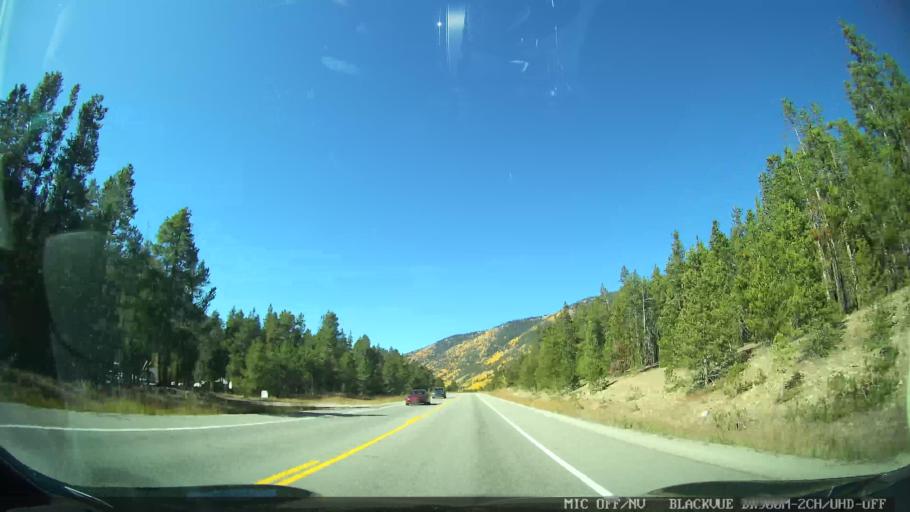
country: US
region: Colorado
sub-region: Lake County
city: Leadville
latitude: 39.3096
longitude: -106.2412
